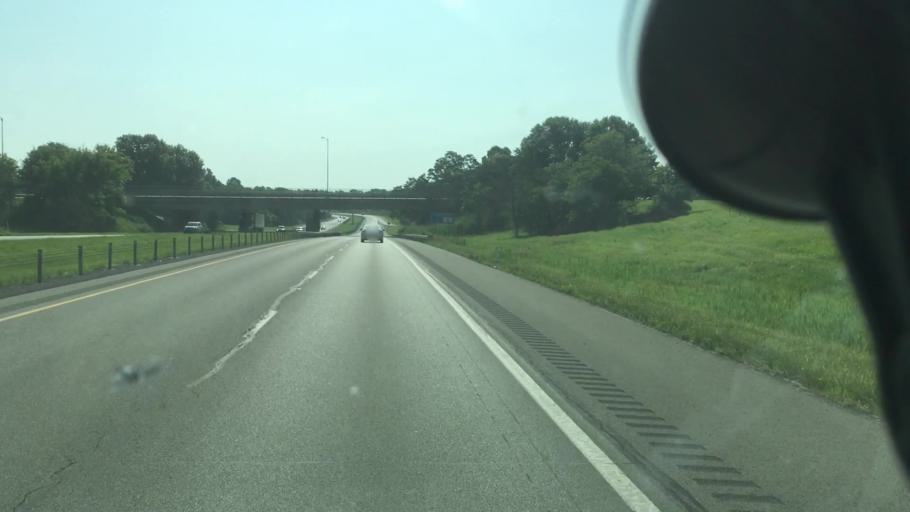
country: US
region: Pennsylvania
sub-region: Lawrence County
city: New Castle
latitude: 40.9723
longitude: -80.3164
